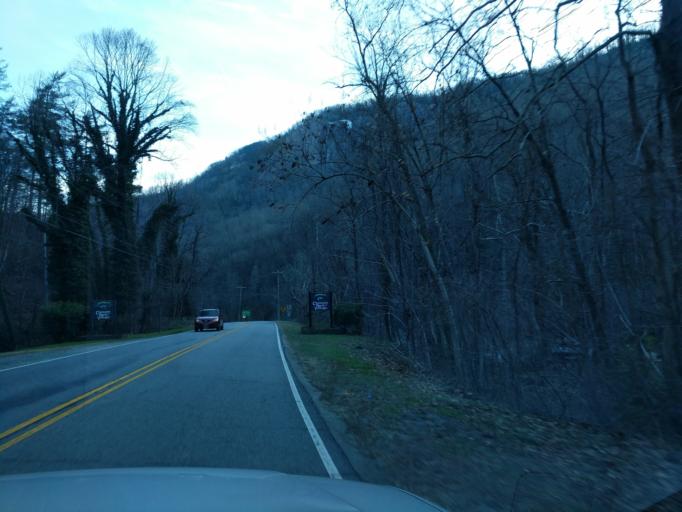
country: US
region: North Carolina
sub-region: Rutherford County
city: Lake Lure
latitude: 35.4481
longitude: -82.2767
